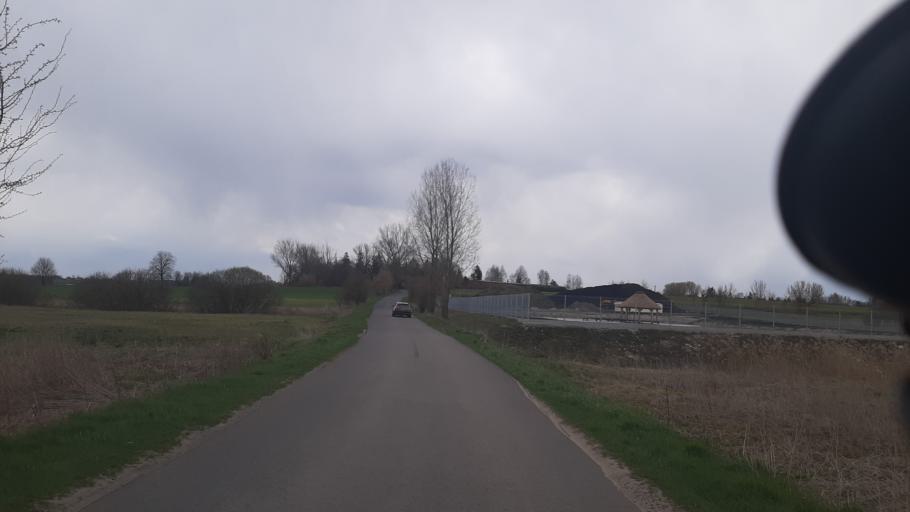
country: PL
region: Lublin Voivodeship
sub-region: Powiat lubelski
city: Niemce
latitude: 51.3679
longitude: 22.5524
